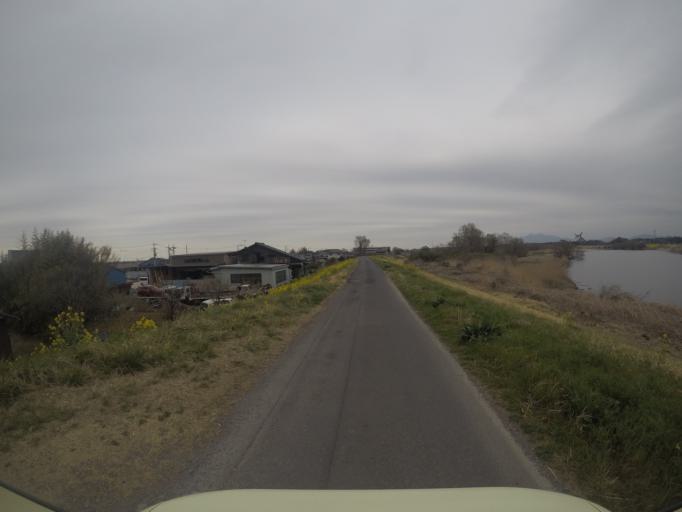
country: JP
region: Ibaraki
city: Mitsukaido
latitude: 36.0658
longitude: 140.0045
